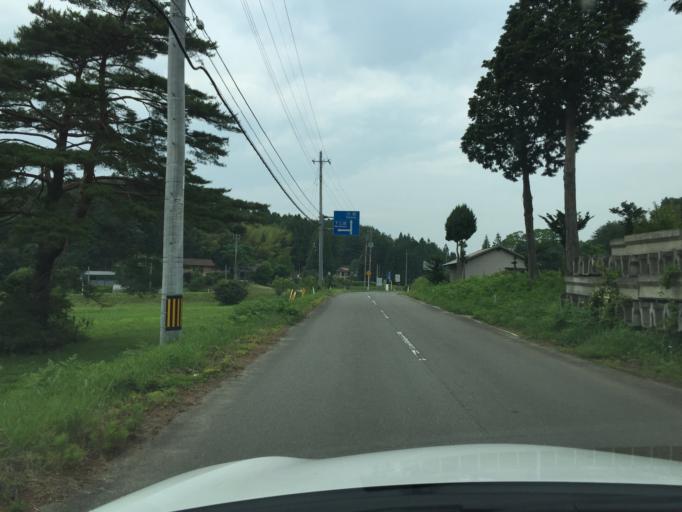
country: JP
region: Fukushima
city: Iwaki
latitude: 37.1995
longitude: 140.7212
